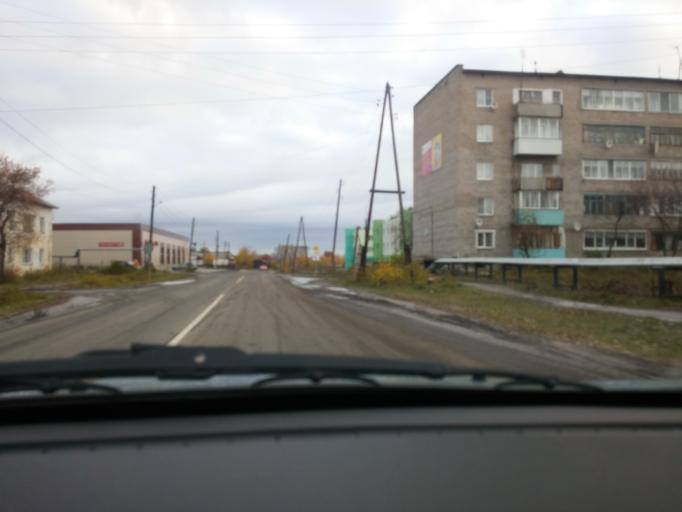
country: RU
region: Sverdlovsk
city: Turinsk
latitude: 58.0403
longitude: 63.7068
